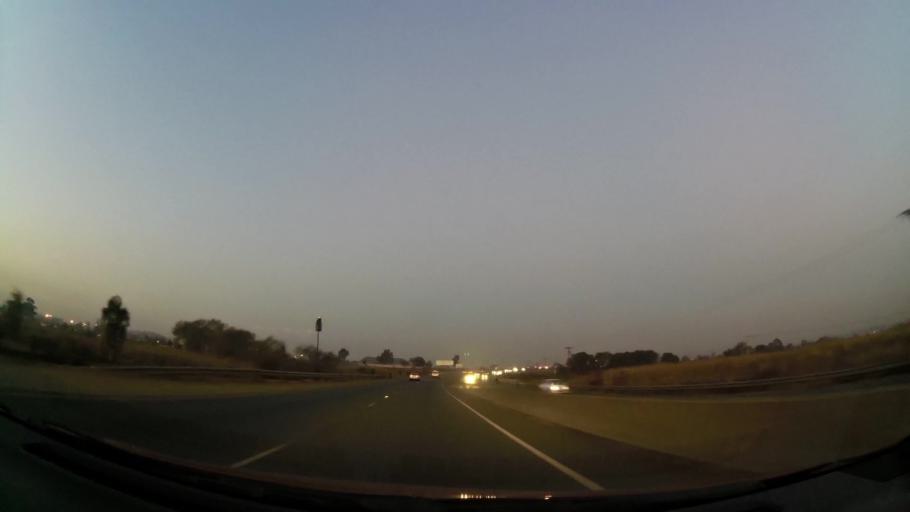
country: ZA
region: Gauteng
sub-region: City of Johannesburg Metropolitan Municipality
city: Soweto
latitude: -26.2946
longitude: 27.8361
